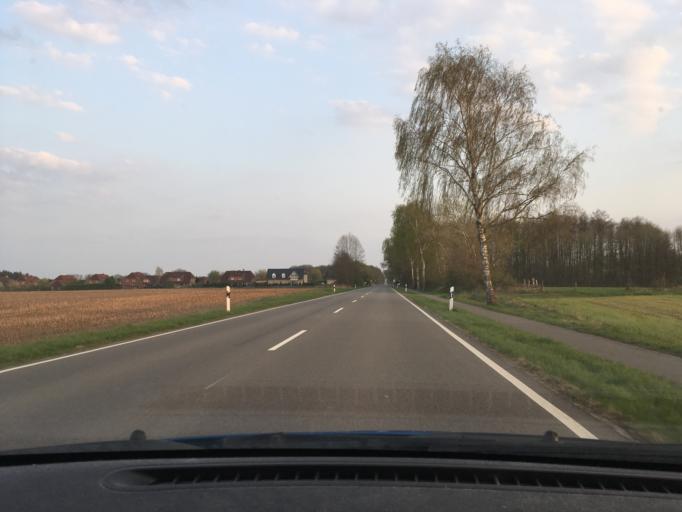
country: DE
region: Lower Saxony
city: Amelinghausen
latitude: 53.1399
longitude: 10.2127
